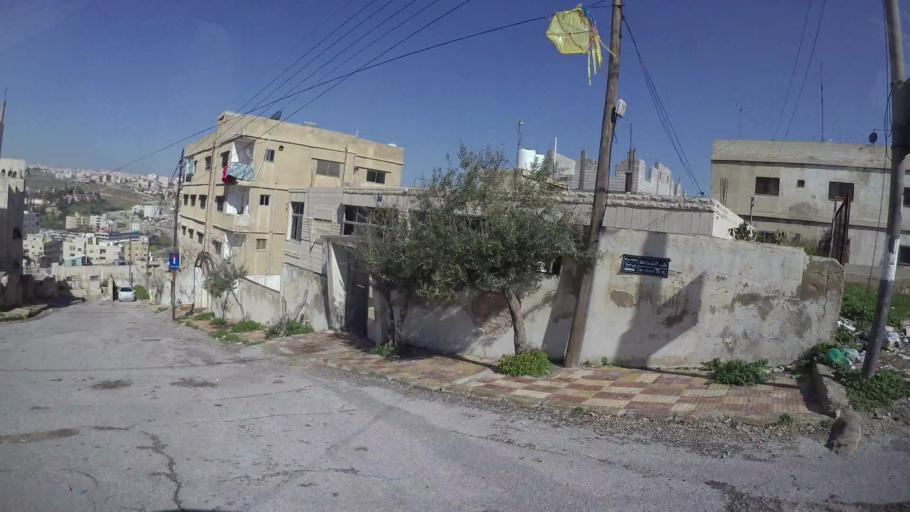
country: JO
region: Amman
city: Amman
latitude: 31.9902
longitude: 35.9845
